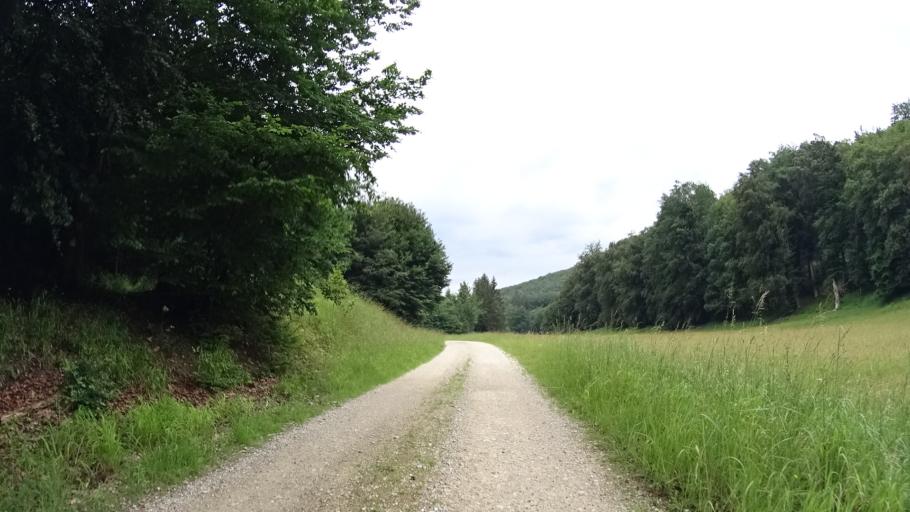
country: DE
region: Bavaria
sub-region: Upper Bavaria
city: Denkendorf
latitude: 48.9161
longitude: 11.5327
